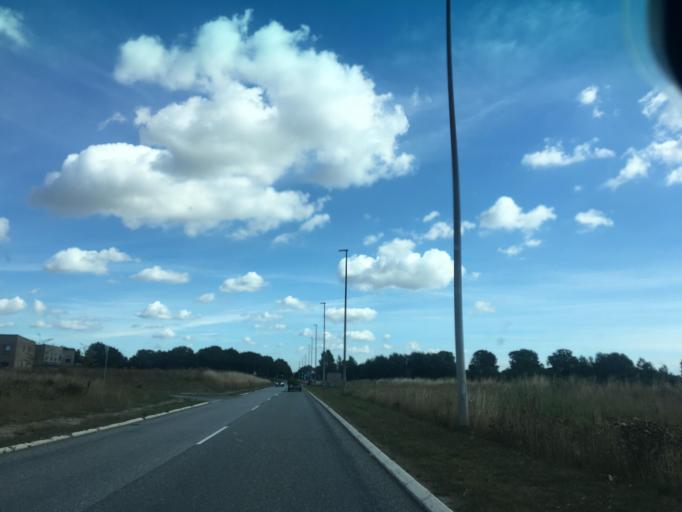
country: DK
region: Zealand
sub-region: Greve Kommune
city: Greve
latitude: 55.5767
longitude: 12.2591
